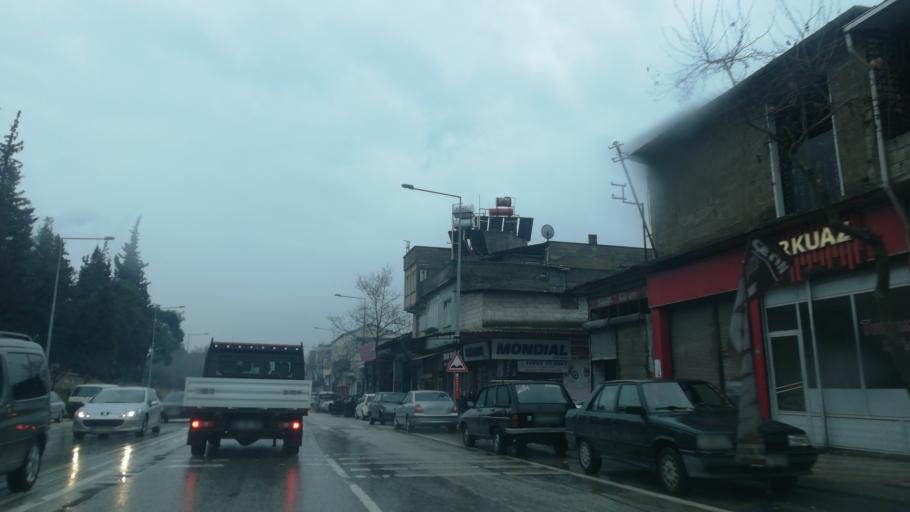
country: TR
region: Kahramanmaras
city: Kahramanmaras
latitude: 37.5750
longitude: 36.9367
